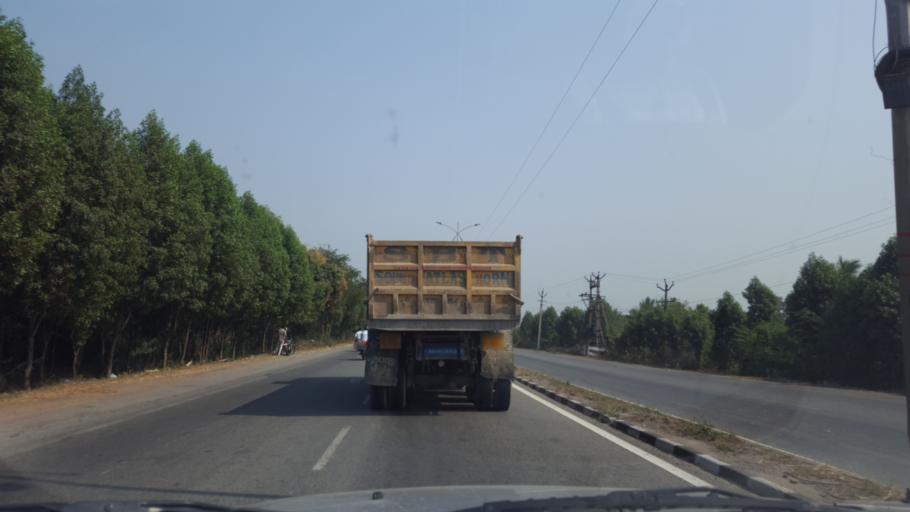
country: IN
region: Andhra Pradesh
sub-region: Vishakhapatnam
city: Anakapalle
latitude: 17.6873
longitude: 83.0784
